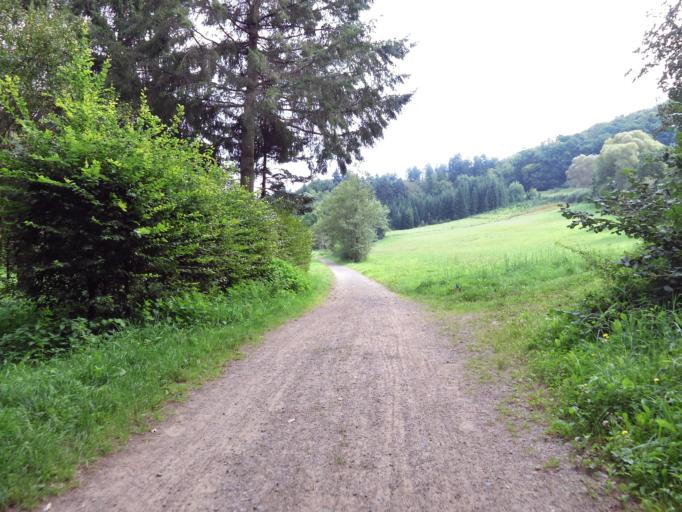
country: DE
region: Rheinland-Pfalz
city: Schweisweiler
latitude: 49.5894
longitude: 7.8308
